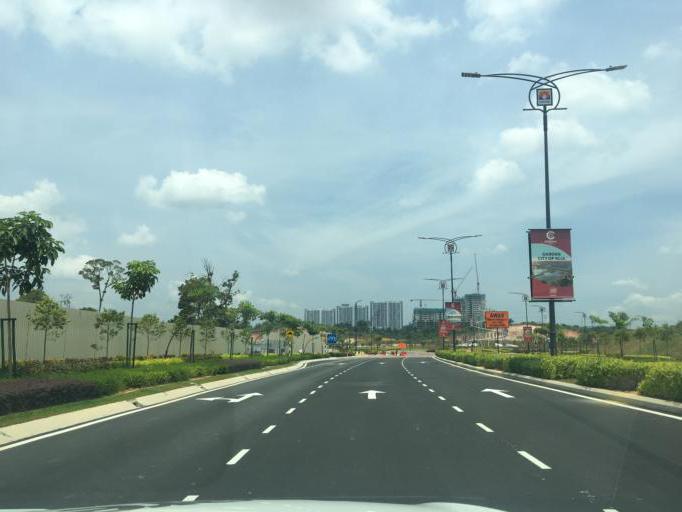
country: MY
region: Putrajaya
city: Putrajaya
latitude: 2.8486
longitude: 101.6974
